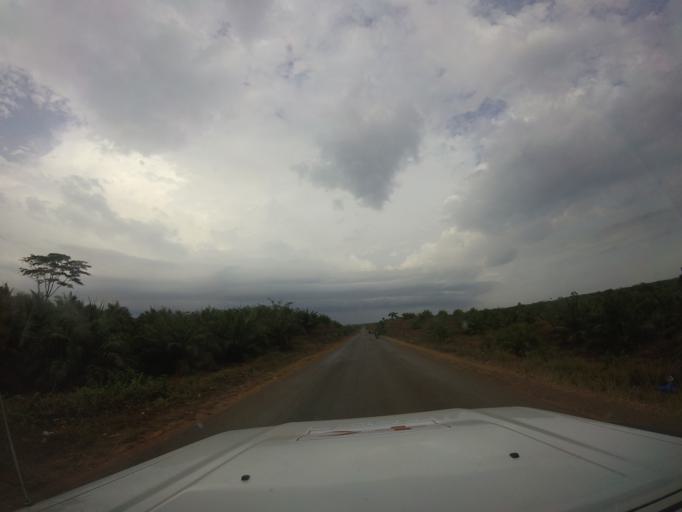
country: LR
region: Bomi
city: Tubmanburg
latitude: 6.7125
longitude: -10.9666
